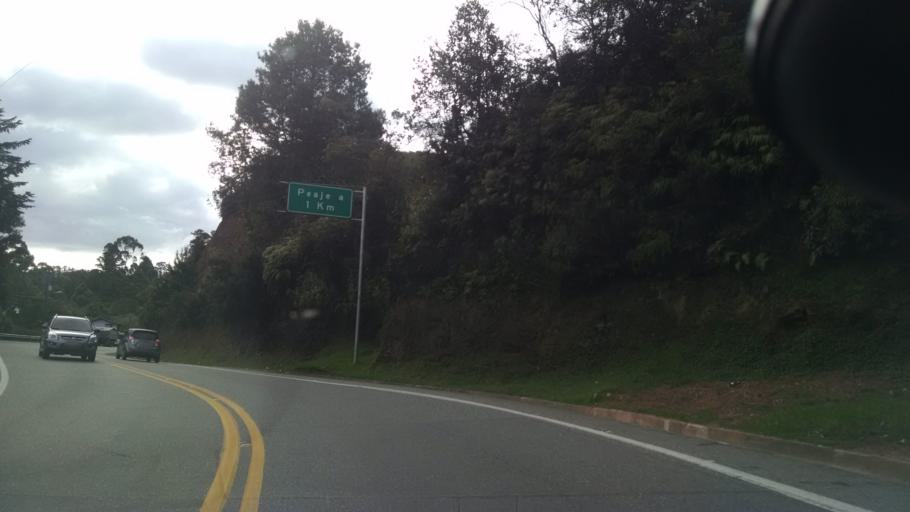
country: CO
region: Antioquia
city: Envigado
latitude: 6.1449
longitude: -75.5255
